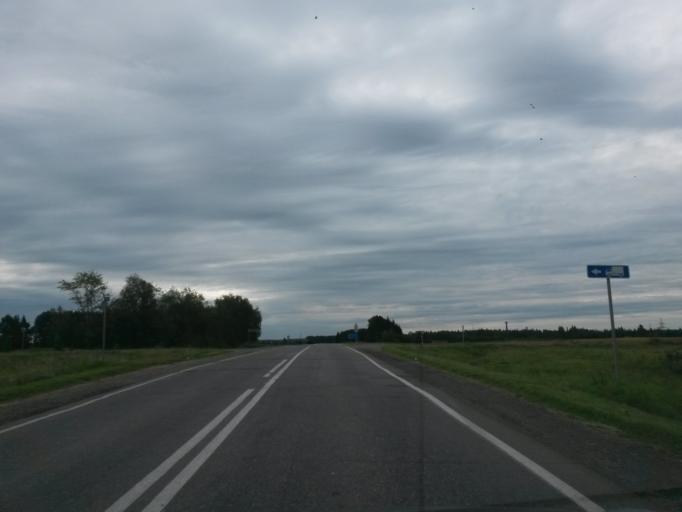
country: RU
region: Jaroslavl
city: Gavrilov-Yam
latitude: 57.3283
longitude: 39.8190
